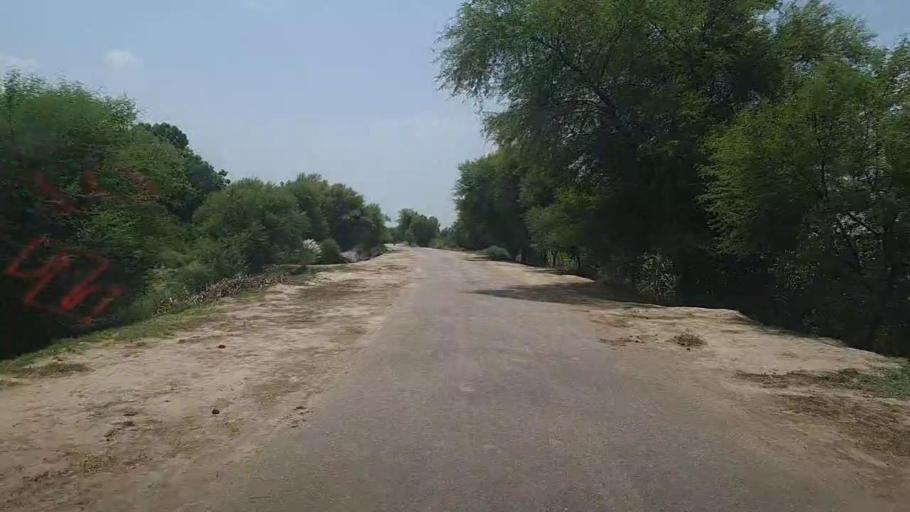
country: PK
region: Sindh
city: Ubauro
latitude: 28.2859
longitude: 69.8089
